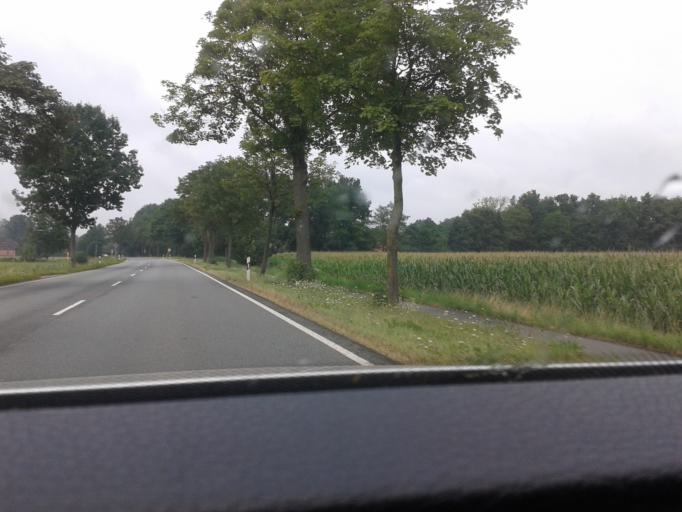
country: DE
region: Lower Saxony
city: Sassenburg
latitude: 52.4838
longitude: 10.6366
